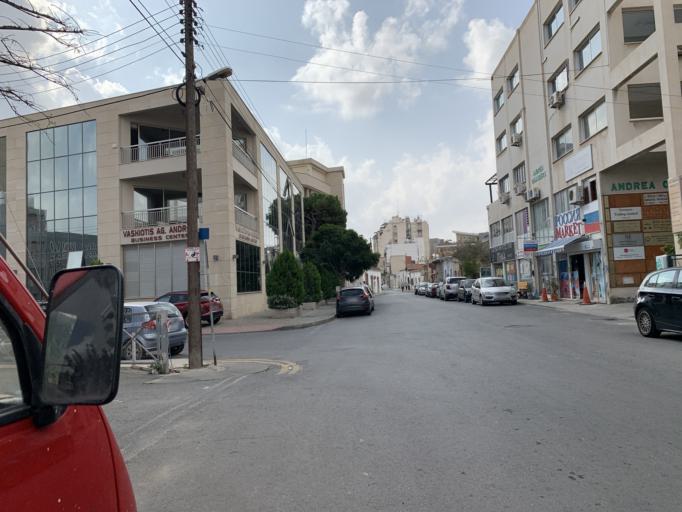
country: CY
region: Limassol
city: Limassol
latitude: 34.6820
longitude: 33.0513
